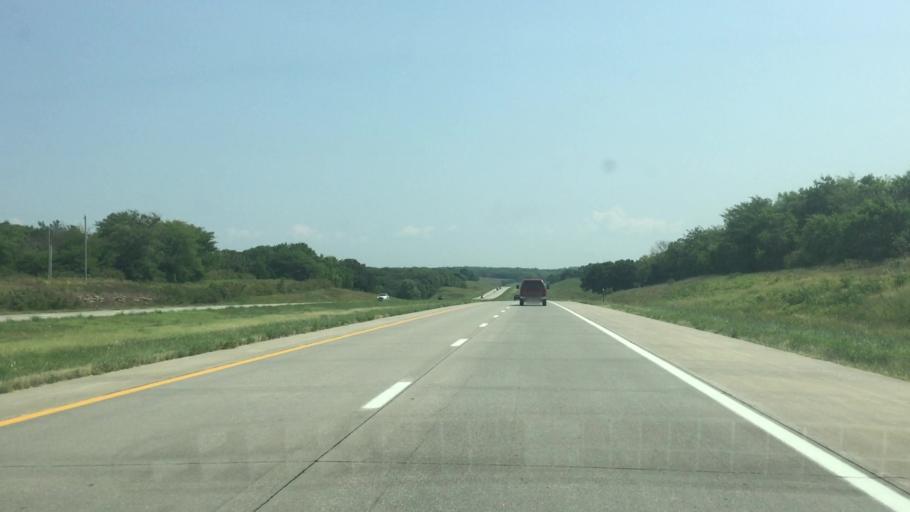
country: US
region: Kansas
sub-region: Osage County
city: Lyndon
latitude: 38.4773
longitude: -95.5058
